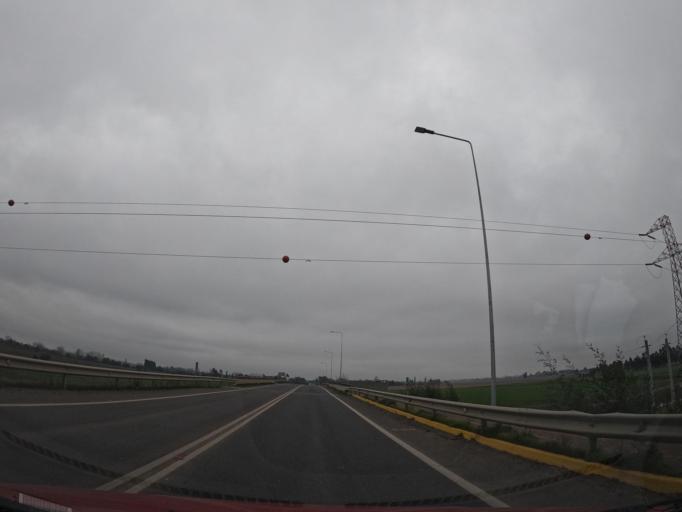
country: CL
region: Maule
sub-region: Provincia de Talca
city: San Clemente
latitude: -35.5157
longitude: -71.4986
